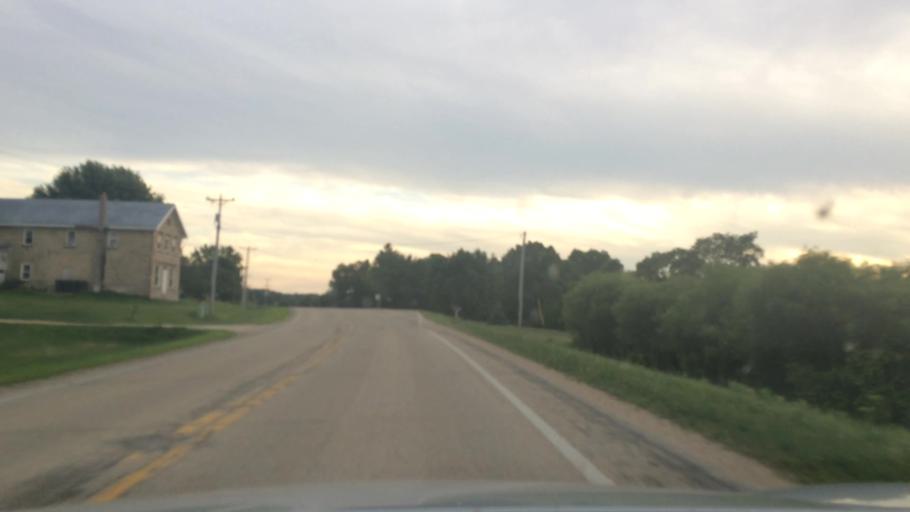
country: US
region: Wisconsin
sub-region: Dane County
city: Waunakee
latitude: 43.1958
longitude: -89.5594
